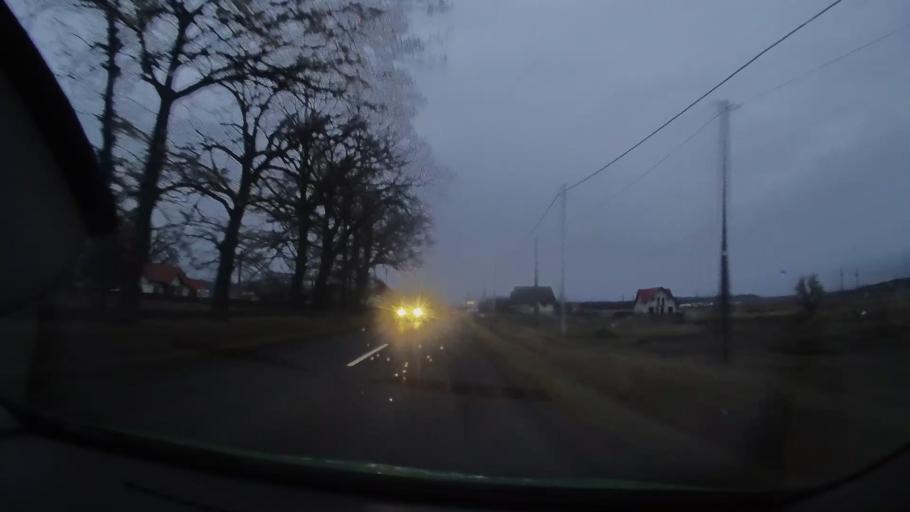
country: RO
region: Mures
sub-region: Comuna Solovastru
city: Solovastru
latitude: 46.7703
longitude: 24.7587
